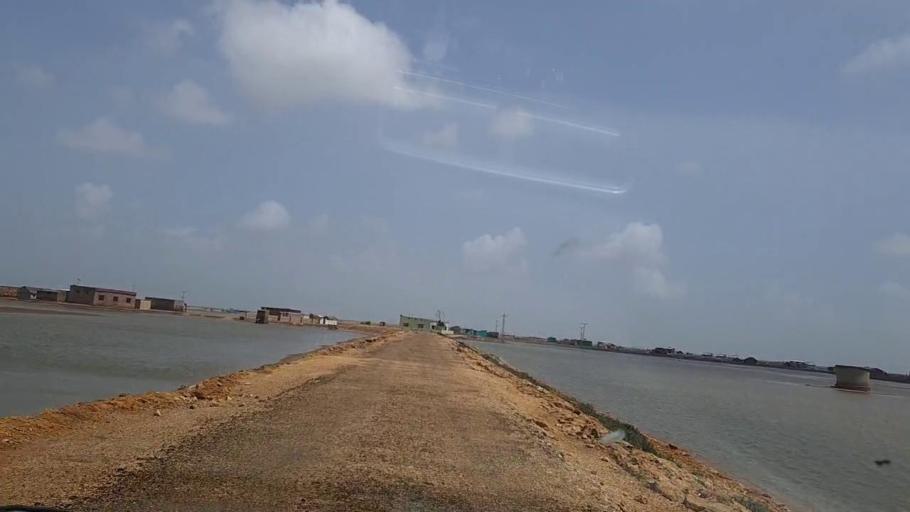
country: PK
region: Sindh
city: Keti Bandar
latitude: 24.1298
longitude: 67.4664
